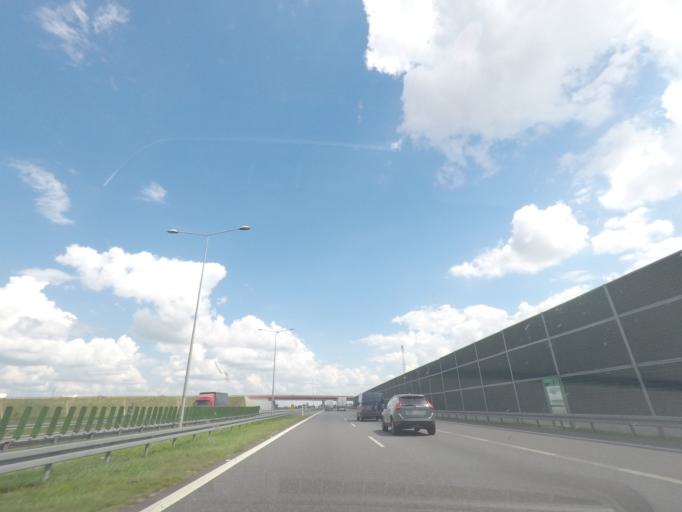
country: PL
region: Masovian Voivodeship
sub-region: Powiat zyrardowski
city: Wiskitki
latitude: 52.0893
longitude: 20.3641
